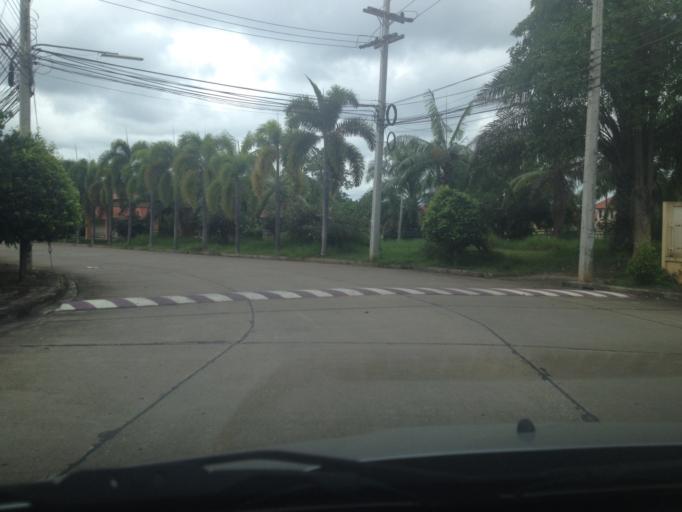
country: TH
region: Chiang Mai
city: Hang Dong
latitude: 18.6974
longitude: 98.9198
